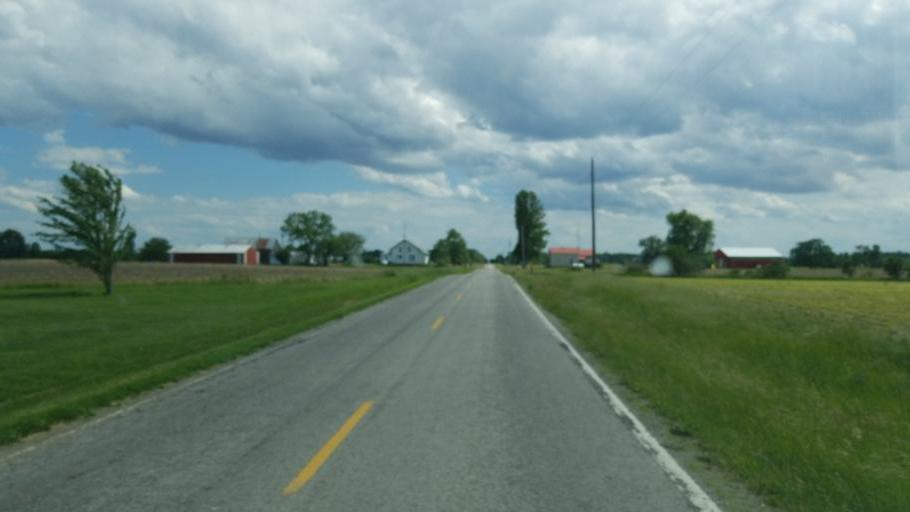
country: US
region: Ohio
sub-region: Huron County
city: Plymouth
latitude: 41.0231
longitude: -82.6074
